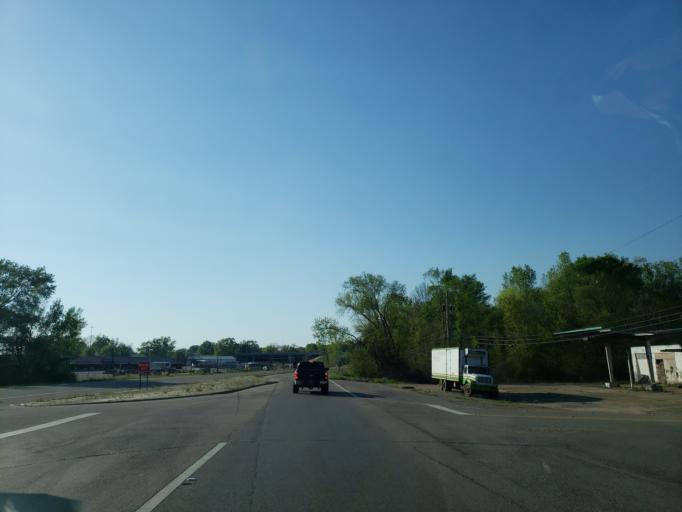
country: US
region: Mississippi
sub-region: Jones County
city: Laurel
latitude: 31.6840
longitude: -89.1214
